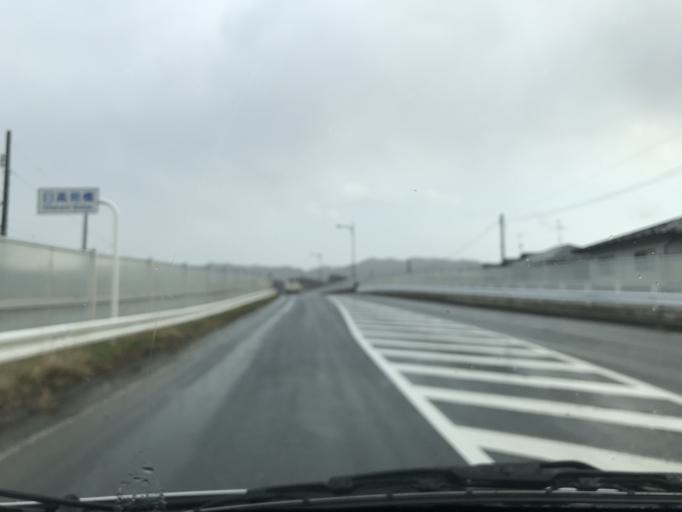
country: JP
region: Iwate
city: Kitakami
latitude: 39.2919
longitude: 141.1378
